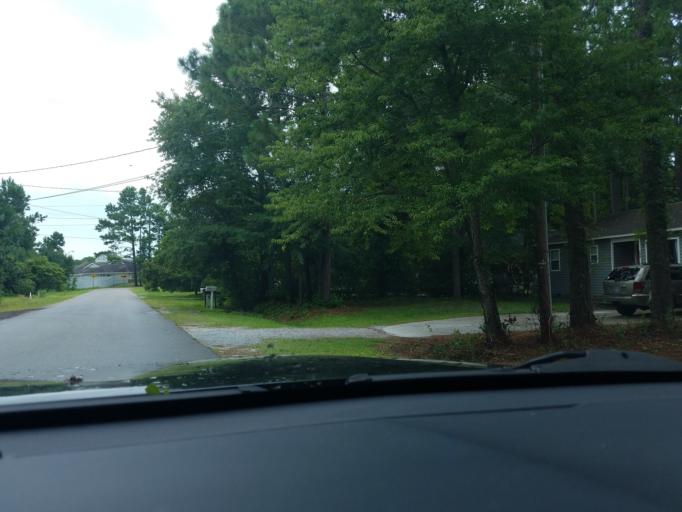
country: US
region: North Carolina
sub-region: New Hanover County
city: Kings Grant
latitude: 34.2399
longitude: -77.8612
